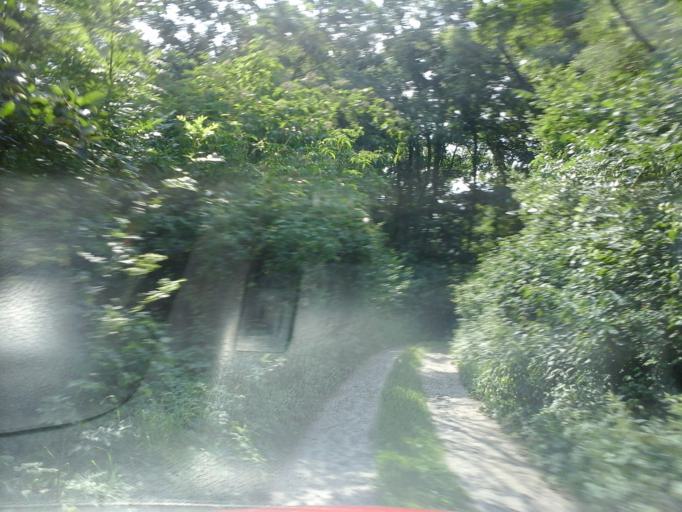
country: PL
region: West Pomeranian Voivodeship
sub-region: Powiat mysliborski
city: Barlinek
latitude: 53.0544
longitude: 15.1940
